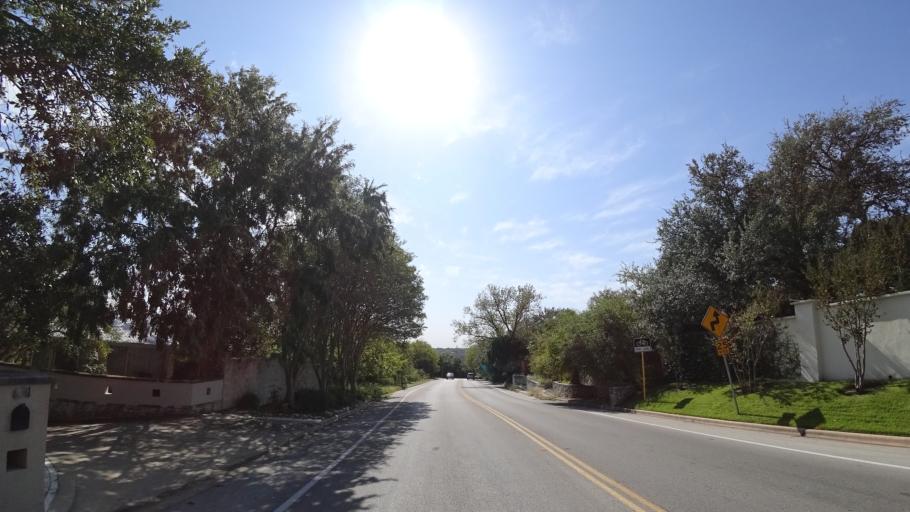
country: US
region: Texas
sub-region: Travis County
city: West Lake Hills
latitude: 30.3513
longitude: -97.7718
